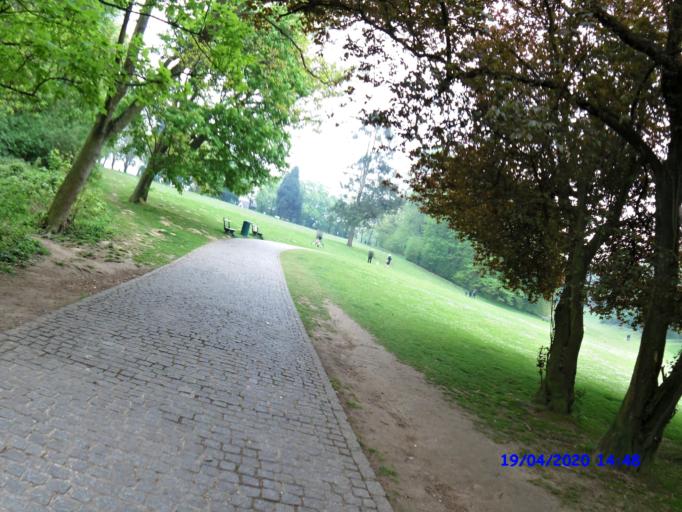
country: BE
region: Flanders
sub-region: Provincie Vlaams-Brabant
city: Kraainem
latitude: 50.8333
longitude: 4.4258
